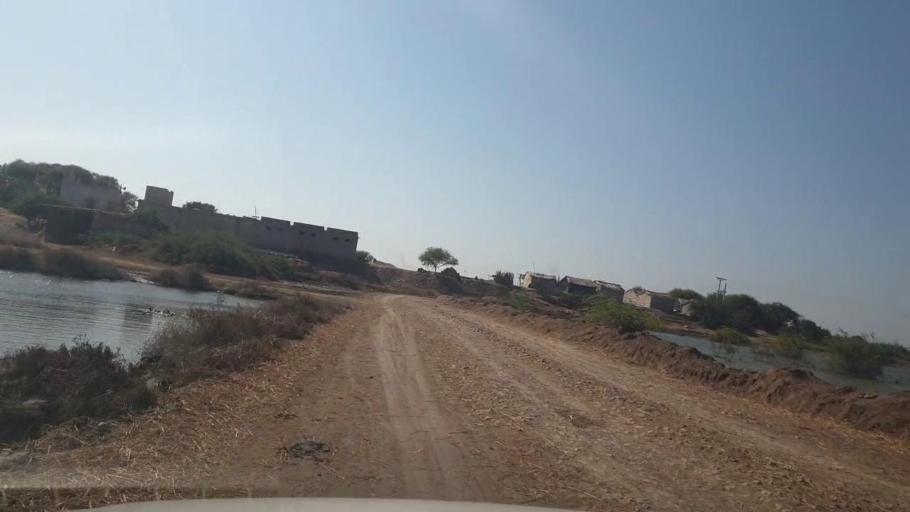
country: PK
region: Sindh
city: Chuhar Jamali
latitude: 24.4404
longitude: 67.8441
